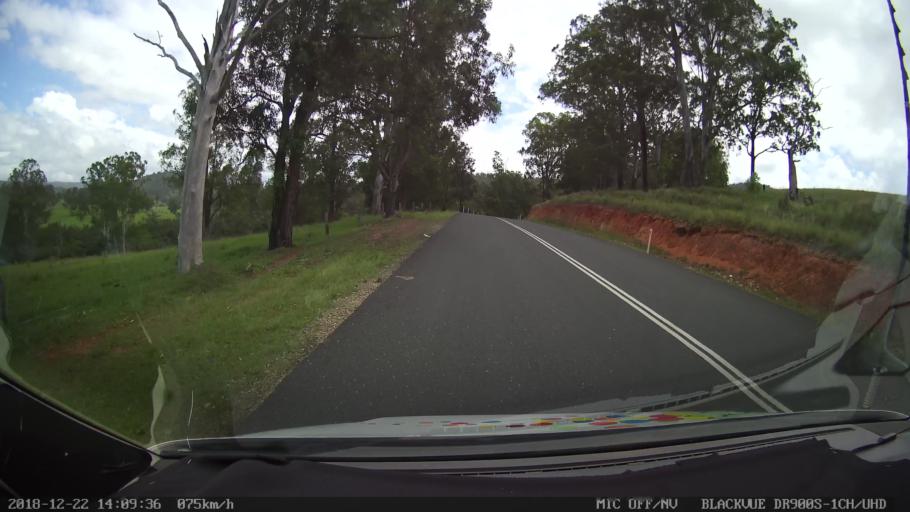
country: AU
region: New South Wales
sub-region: Clarence Valley
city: Coutts Crossing
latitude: -29.9880
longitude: 152.7160
